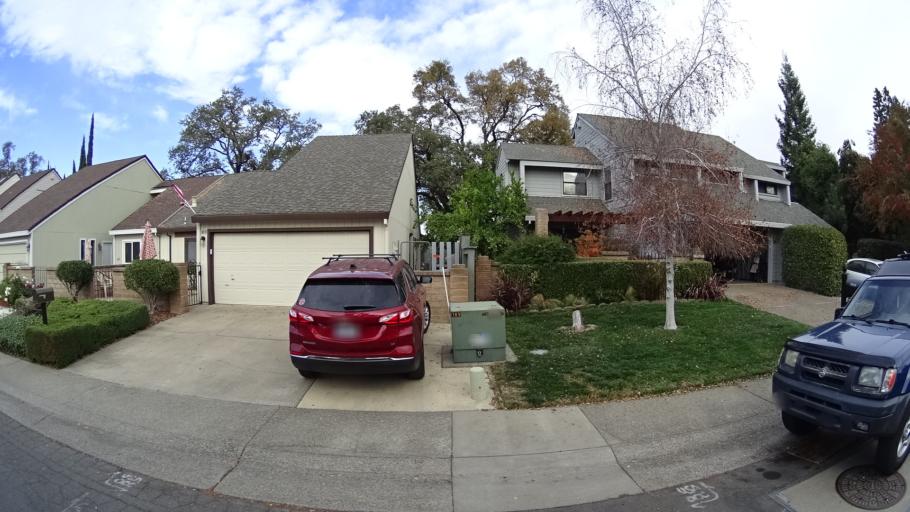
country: US
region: California
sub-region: Sacramento County
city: Fair Oaks
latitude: 38.6709
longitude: -121.2657
